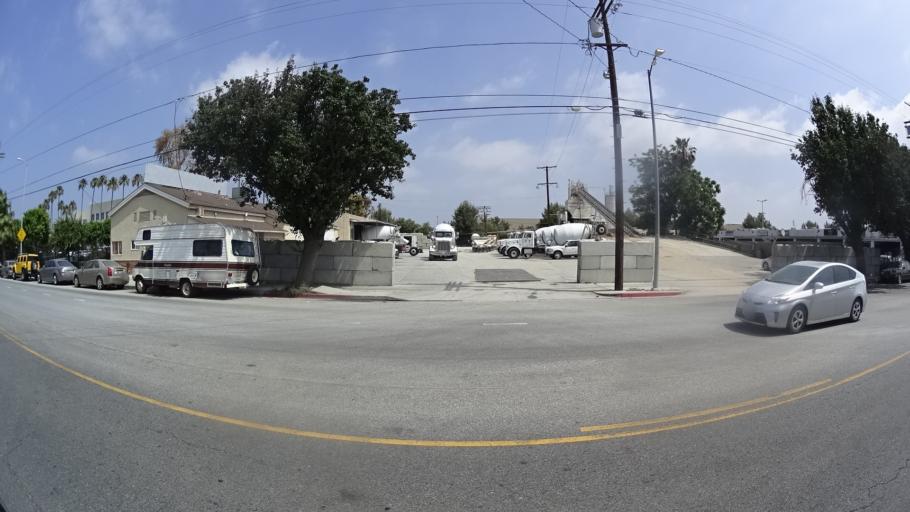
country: US
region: California
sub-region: Los Angeles County
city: Van Nuys
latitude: 34.1793
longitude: -118.4647
